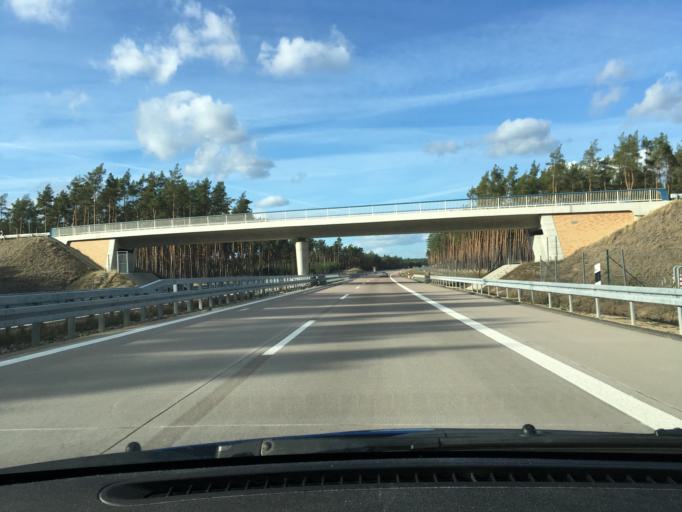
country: DE
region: Mecklenburg-Vorpommern
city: Grabow
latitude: 53.2625
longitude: 11.5339
